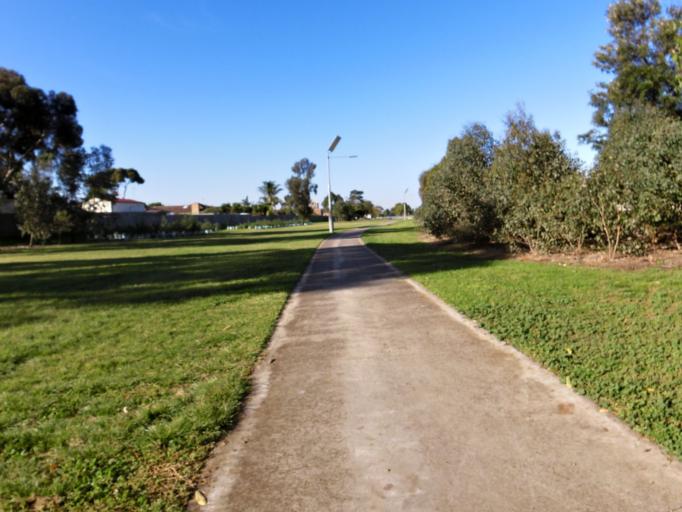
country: AU
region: Victoria
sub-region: Wyndham
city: Hoppers Crossing
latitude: -37.8694
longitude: 144.7000
